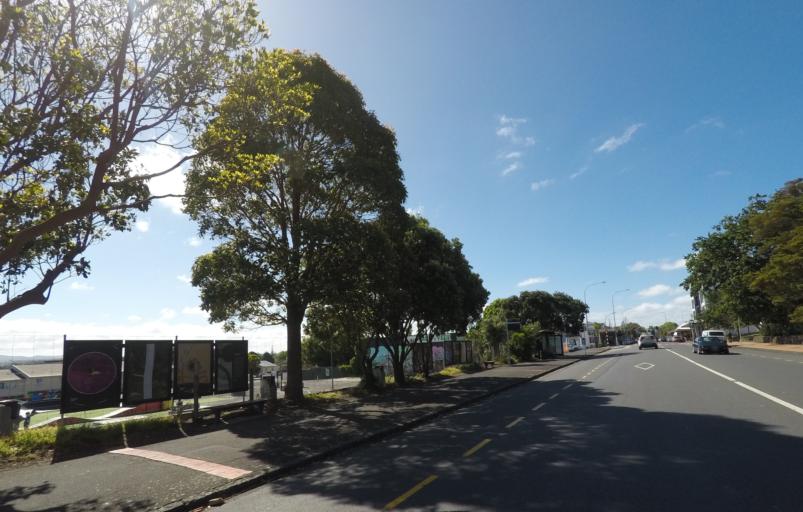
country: NZ
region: Auckland
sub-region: Auckland
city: Rosebank
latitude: -36.8964
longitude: 174.6971
